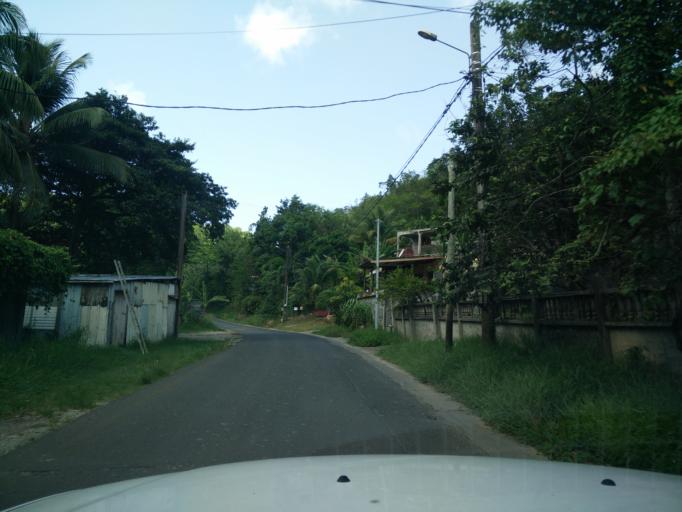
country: GP
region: Guadeloupe
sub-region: Guadeloupe
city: Le Gosier
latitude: 16.2229
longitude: -61.4728
